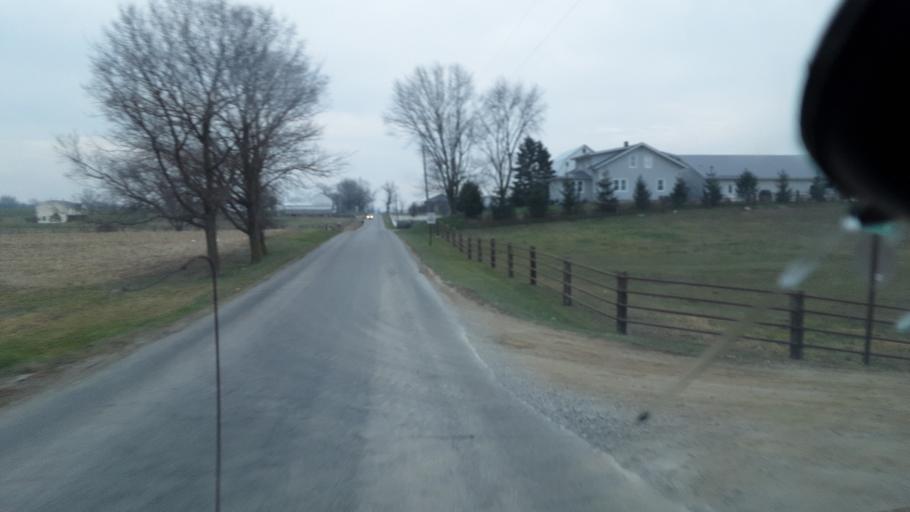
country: US
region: Indiana
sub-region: Elkhart County
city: Middlebury
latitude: 41.6870
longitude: -85.6198
